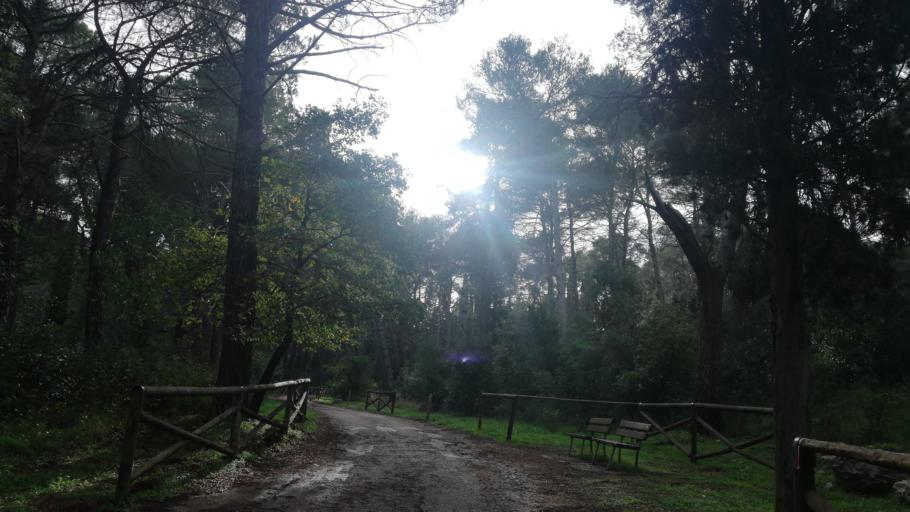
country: IT
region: Apulia
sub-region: Provincia di Bari
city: Cassano delle Murge
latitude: 40.8897
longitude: 16.6998
